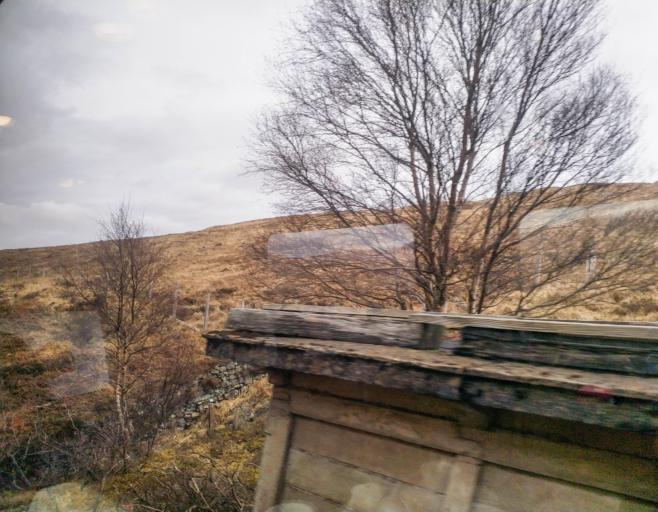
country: GB
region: Scotland
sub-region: Highland
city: Spean Bridge
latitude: 56.5412
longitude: -4.7588
